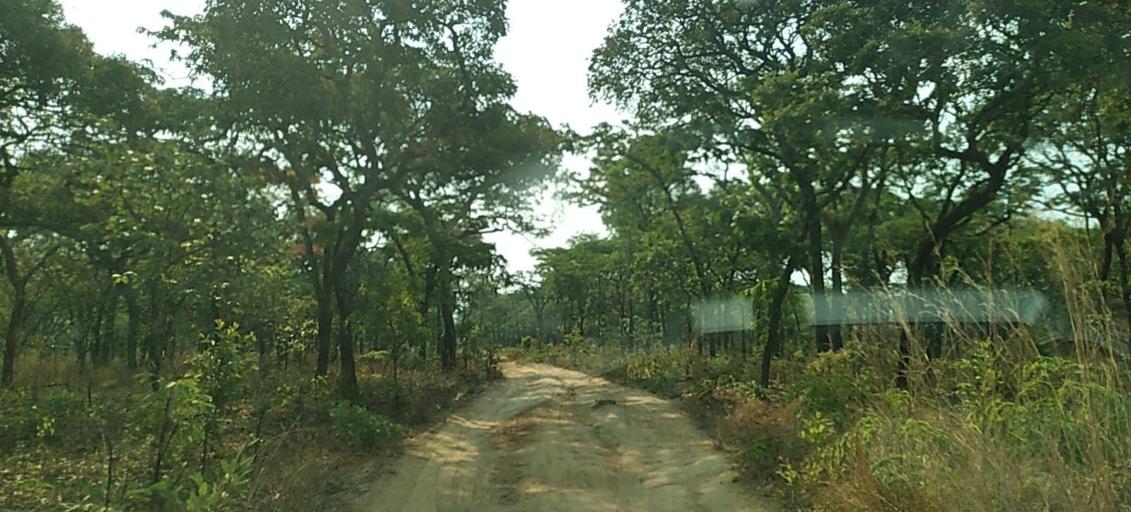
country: ZM
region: North-Western
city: Solwezi
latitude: -12.0712
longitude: 26.2276
